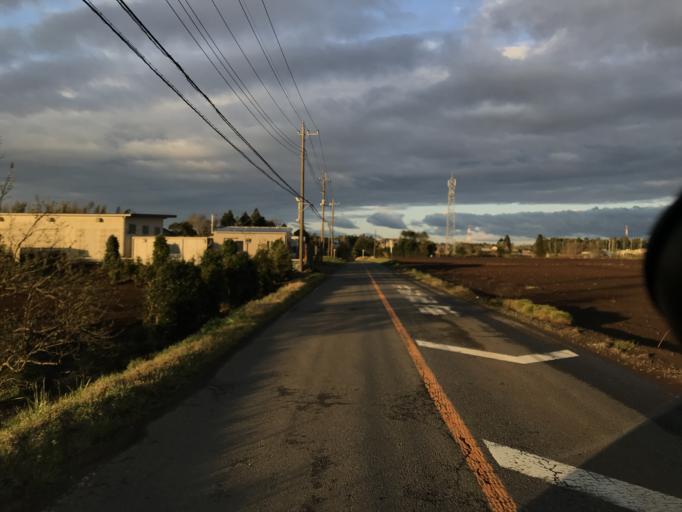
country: JP
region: Chiba
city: Sawara
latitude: 35.8133
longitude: 140.4537
